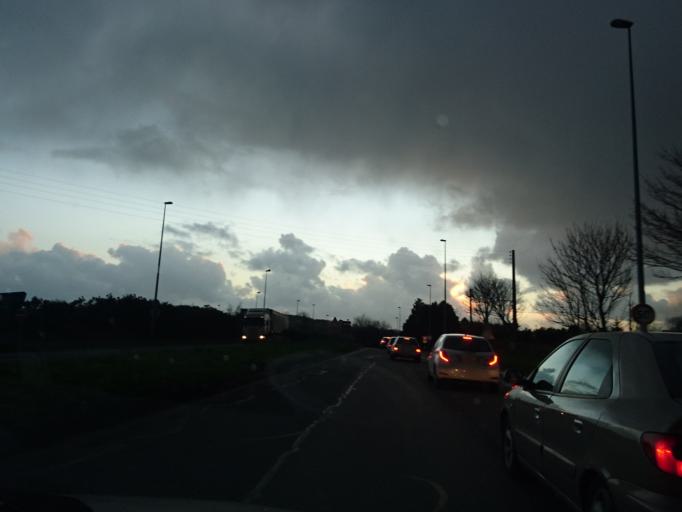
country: FR
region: Brittany
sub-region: Departement du Finistere
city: Guipavas
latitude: 48.4192
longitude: -4.4280
